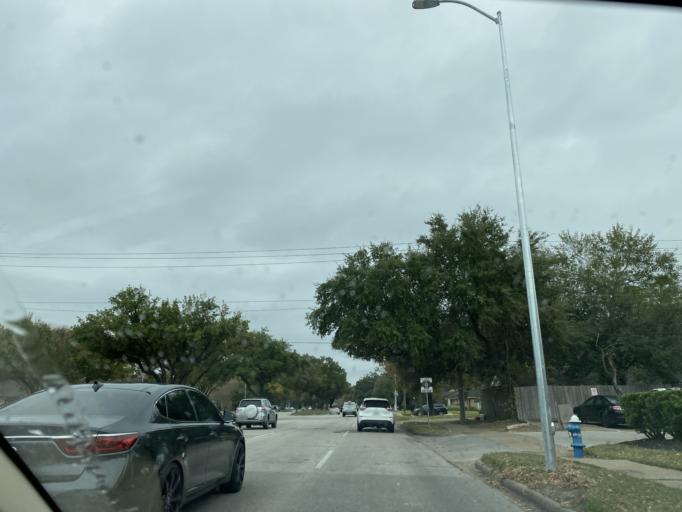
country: US
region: Texas
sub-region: Harris County
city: Piney Point Village
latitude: 29.7292
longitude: -95.5113
